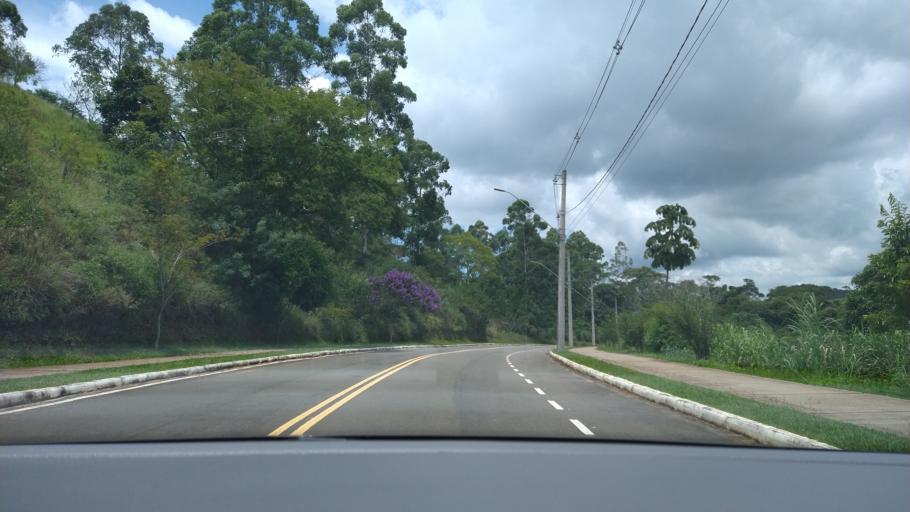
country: BR
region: Minas Gerais
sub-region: Vicosa
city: Vicosa
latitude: -20.7635
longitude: -42.8583
